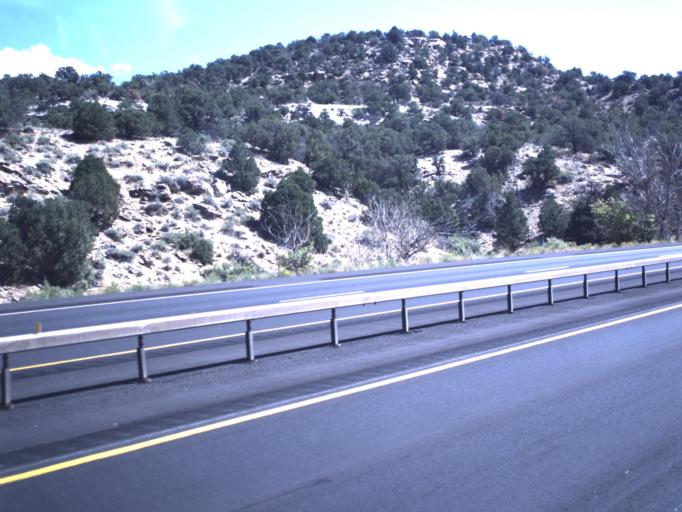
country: US
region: Utah
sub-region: Sevier County
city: Salina
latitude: 38.9149
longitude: -111.7192
